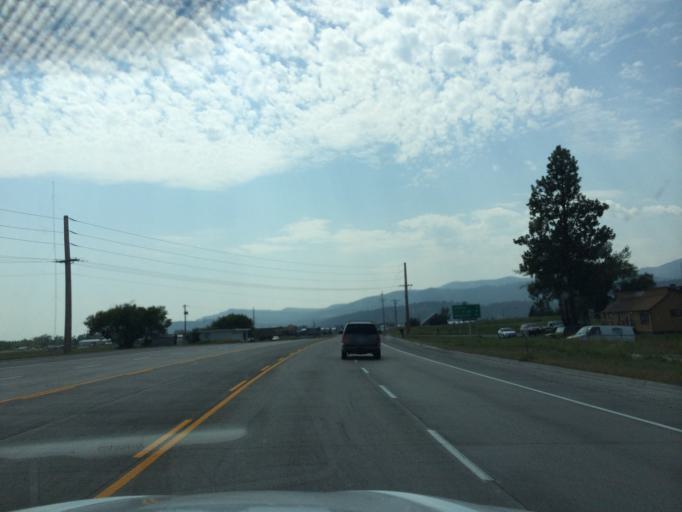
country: US
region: Montana
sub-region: Flathead County
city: Kalispell
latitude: 48.1630
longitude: -114.2879
